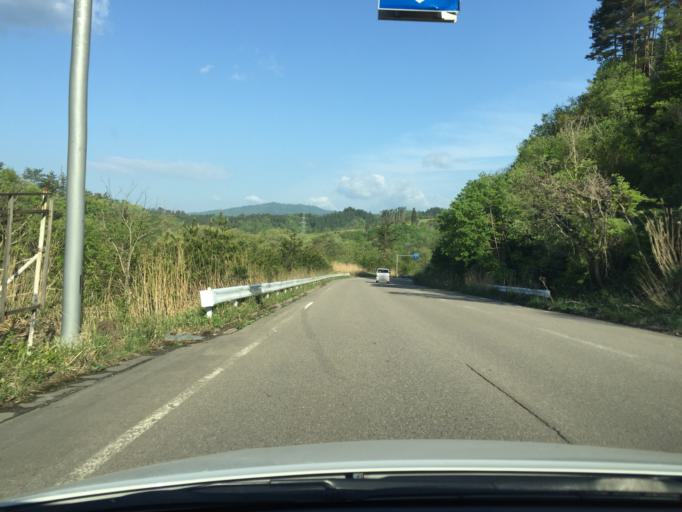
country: JP
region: Fukushima
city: Kitakata
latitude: 37.6687
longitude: 139.8213
